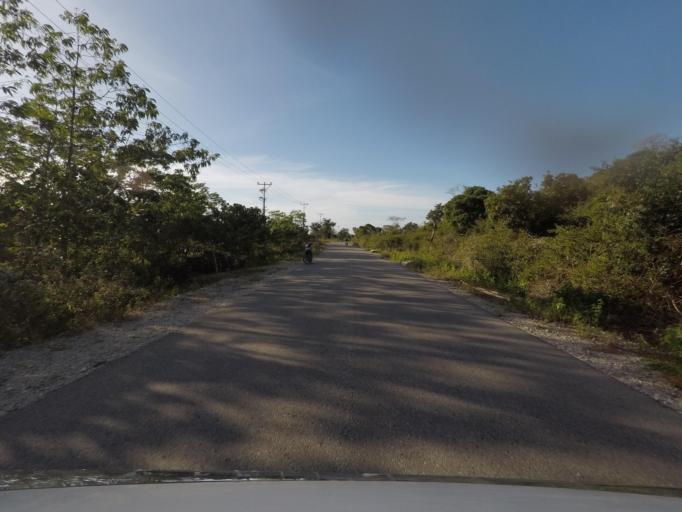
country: TL
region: Lautem
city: Lospalos
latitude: -8.3795
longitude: 127.0149
